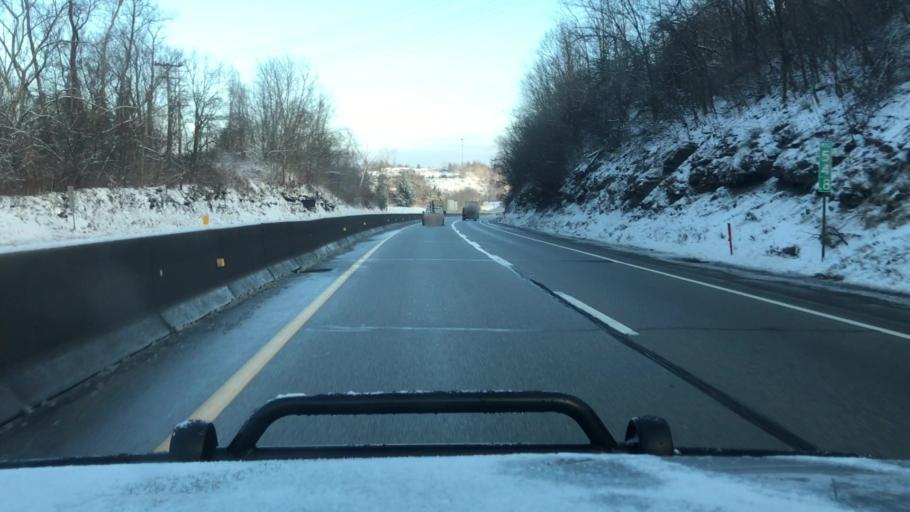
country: US
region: Pennsylvania
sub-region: Allegheny County
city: Plum
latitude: 40.4596
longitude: -79.7591
